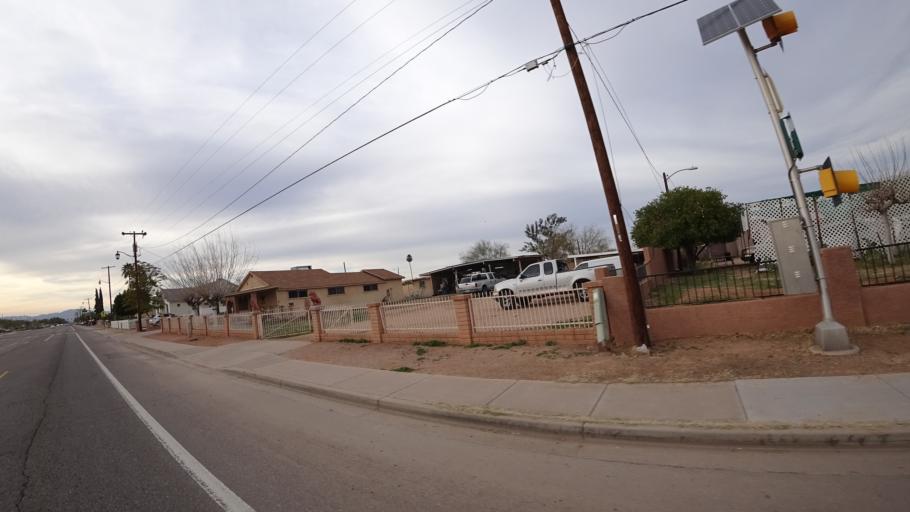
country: US
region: Arizona
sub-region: Maricopa County
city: Surprise
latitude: 33.6236
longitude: -112.3365
